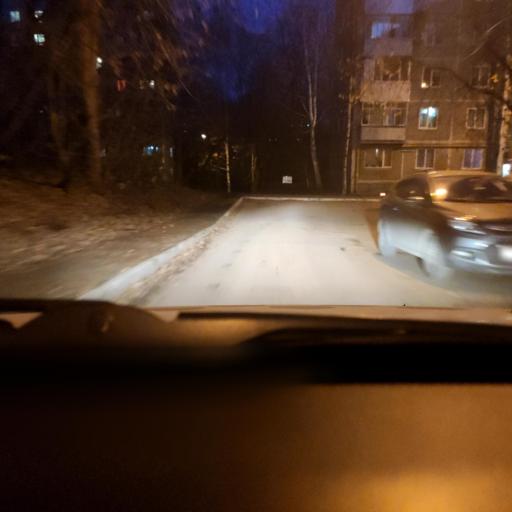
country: RU
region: Perm
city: Perm
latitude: 57.9828
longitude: 56.2238
